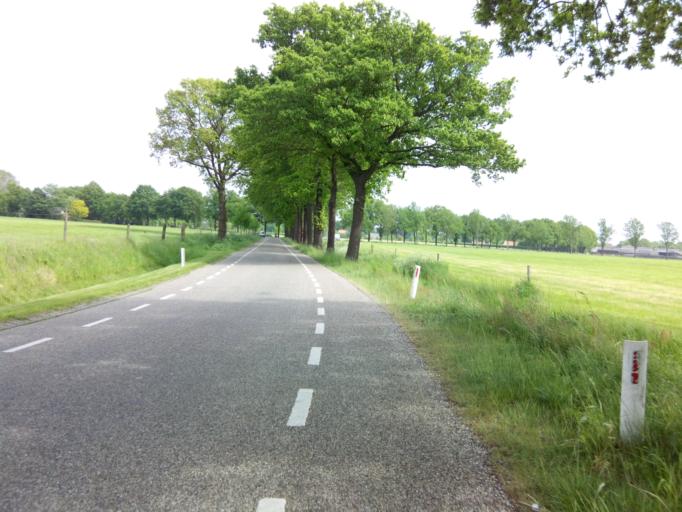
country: NL
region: Gelderland
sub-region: Berkelland
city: Eibergen
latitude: 52.0662
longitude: 6.5851
